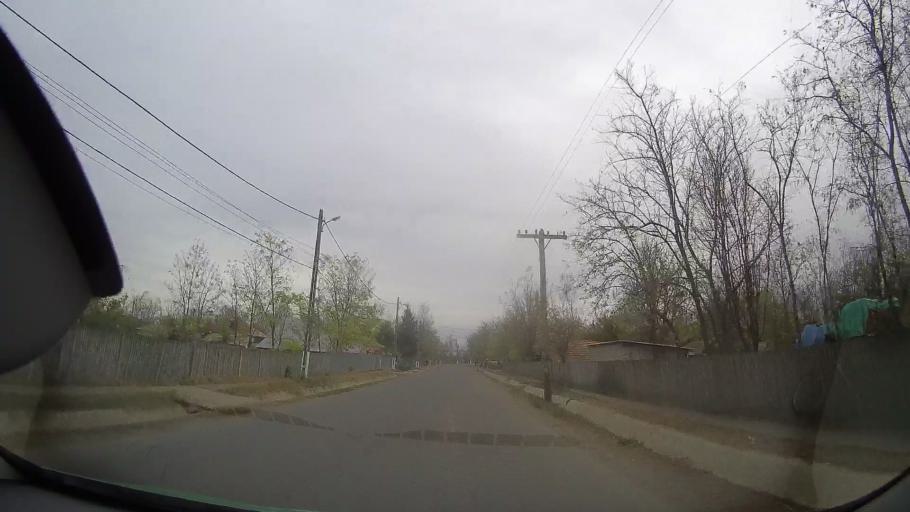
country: RO
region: Braila
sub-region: Comuna Rosiori
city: Rosiori
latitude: 44.8073
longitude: 27.3798
